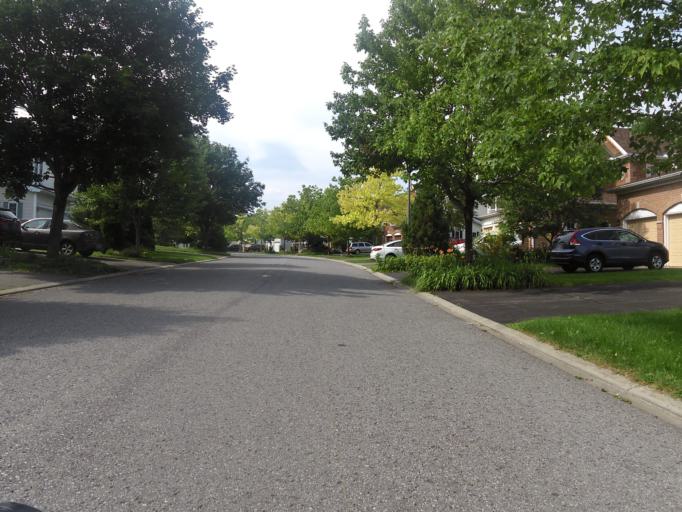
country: CA
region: Ontario
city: Bells Corners
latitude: 45.3129
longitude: -75.9215
